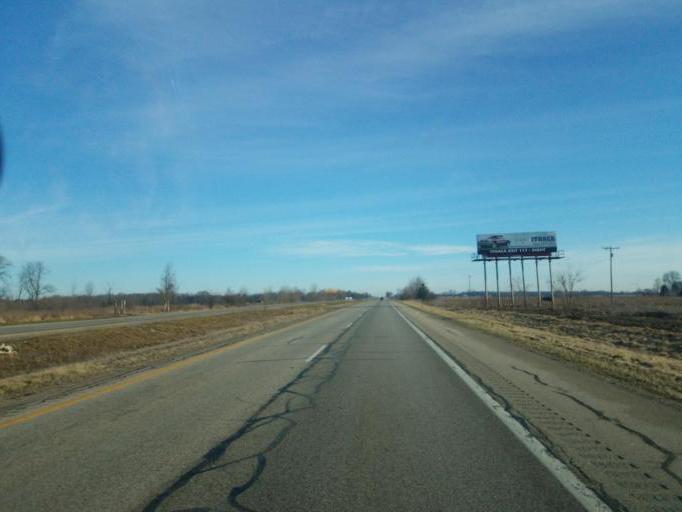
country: US
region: Michigan
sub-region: Gratiot County
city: Ithaca
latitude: 43.2143
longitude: -84.5632
